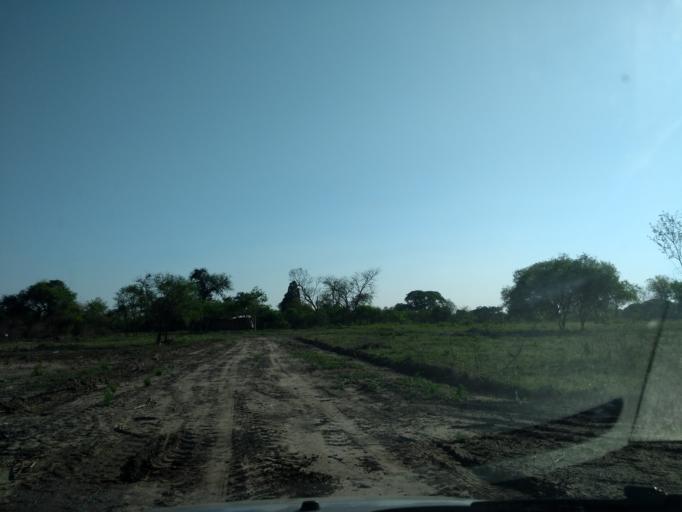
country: AR
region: Chaco
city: Fontana
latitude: -27.4192
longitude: -59.0545
